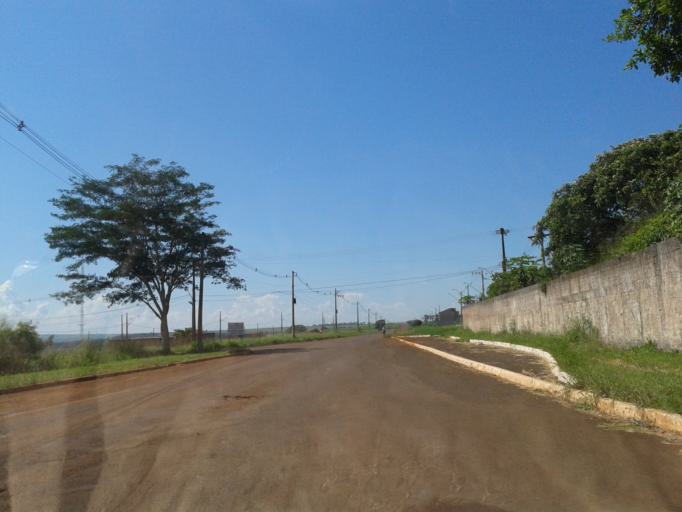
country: BR
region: Goias
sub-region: Itumbiara
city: Itumbiara
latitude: -18.4274
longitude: -49.1868
